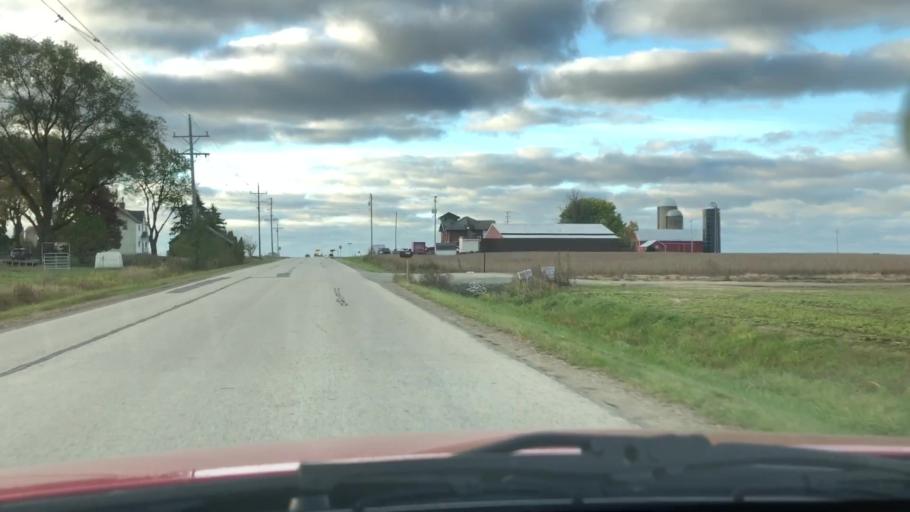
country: US
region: Wisconsin
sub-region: Outagamie County
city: Seymour
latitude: 44.5023
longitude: -88.3104
